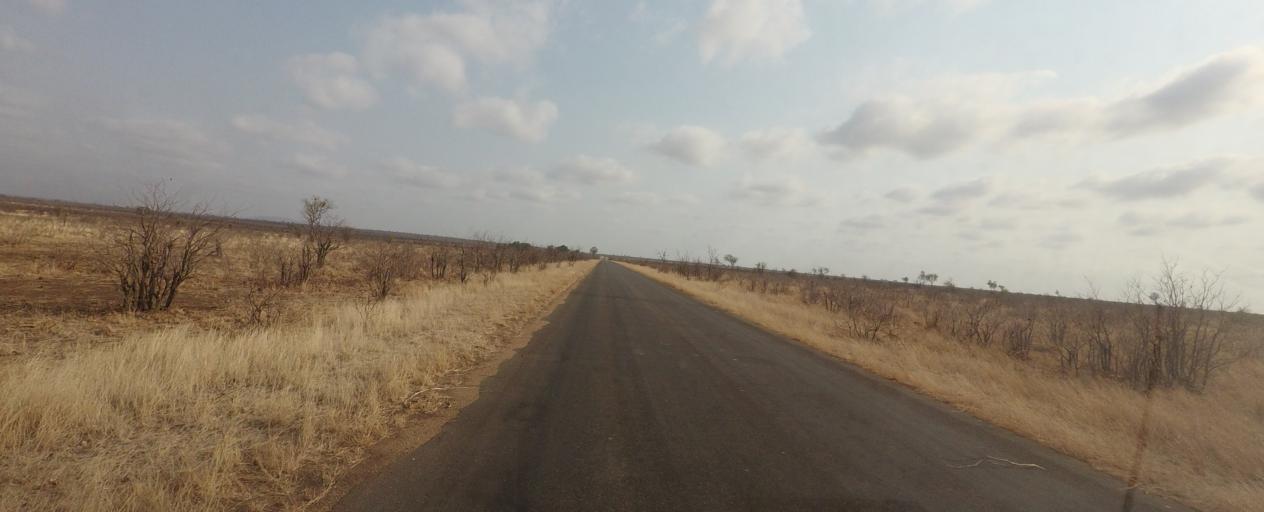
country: ZA
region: Limpopo
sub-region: Vhembe District Municipality
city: Mutale
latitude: -22.9131
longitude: 31.2529
